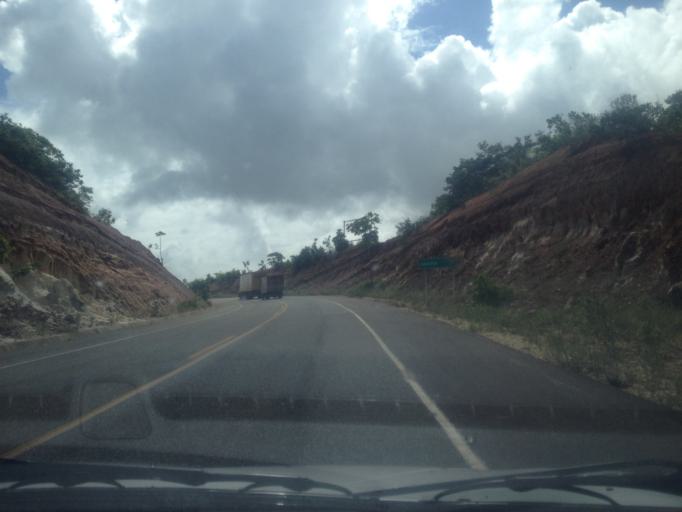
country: BR
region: Sergipe
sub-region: Indiaroba
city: Indiaroba
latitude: -11.5754
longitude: -37.5467
